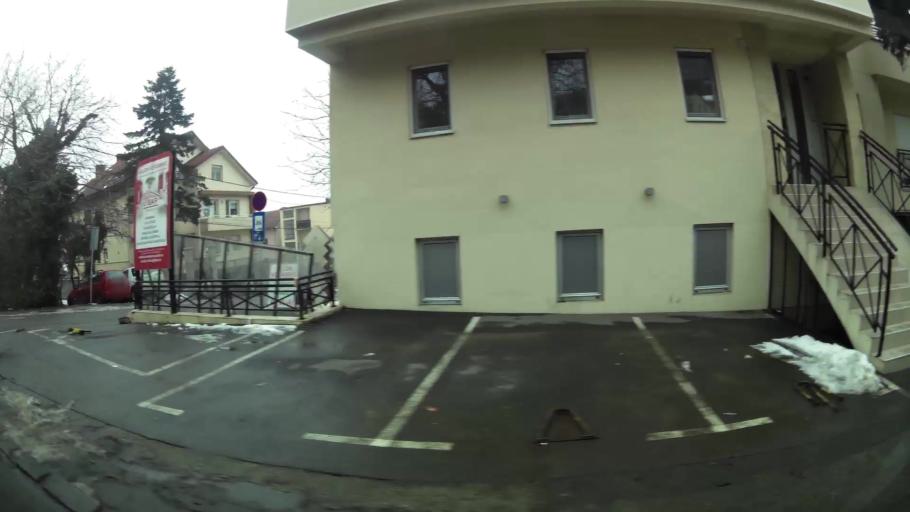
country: RS
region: Central Serbia
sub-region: Belgrade
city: Vozdovac
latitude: 44.7780
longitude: 20.4766
